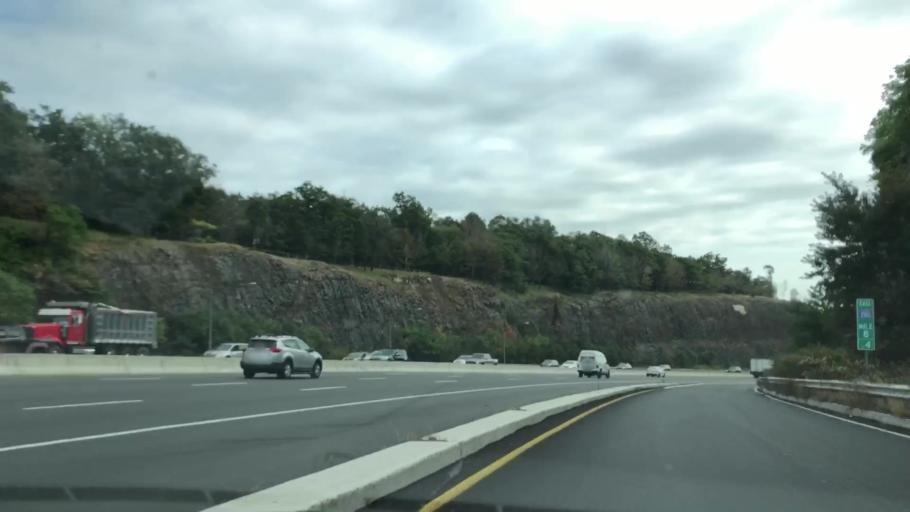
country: US
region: New Jersey
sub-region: Essex County
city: West Orange
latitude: 40.7955
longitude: -74.2497
